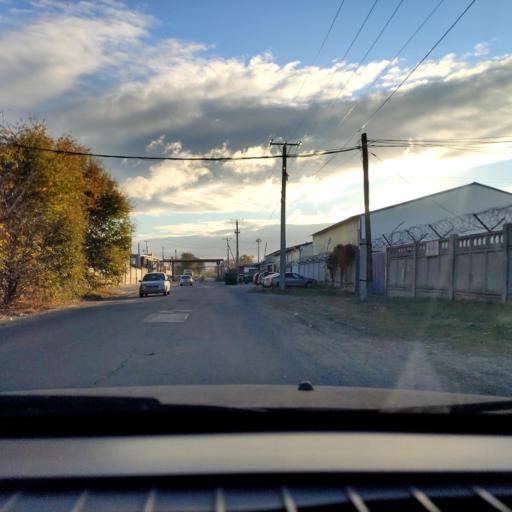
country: RU
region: Samara
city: Tol'yatti
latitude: 53.5757
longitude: 49.2800
